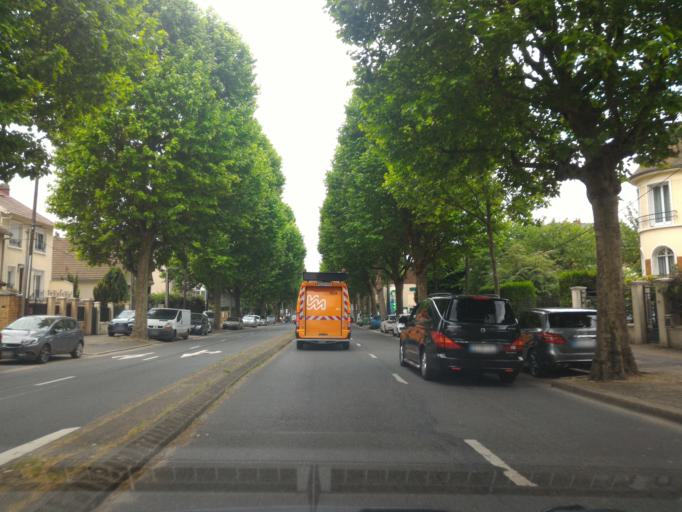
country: FR
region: Ile-de-France
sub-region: Departement du Val-de-Marne
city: L'Hay-les-Roses
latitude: 48.7780
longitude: 2.3405
